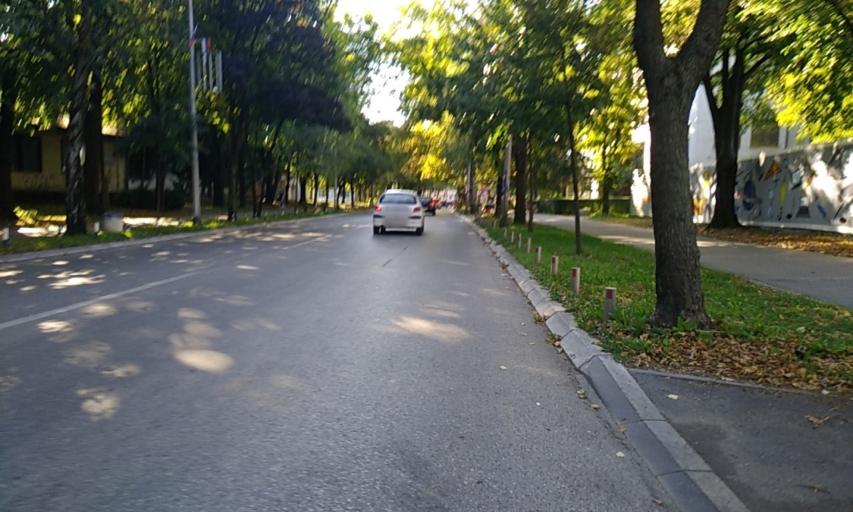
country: BA
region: Republika Srpska
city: Banja Luka
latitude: 44.7758
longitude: 17.1907
